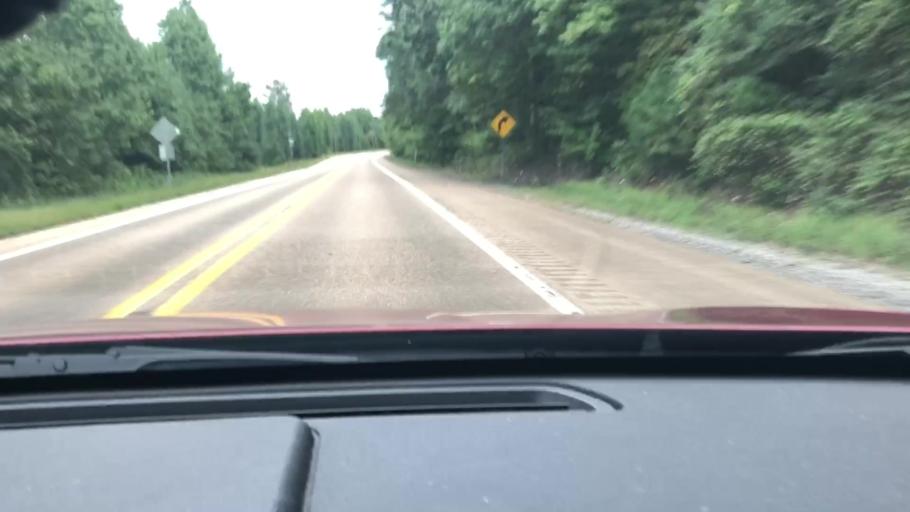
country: US
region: Arkansas
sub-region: Miller County
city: Texarkana
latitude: 33.4193
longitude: -93.8183
